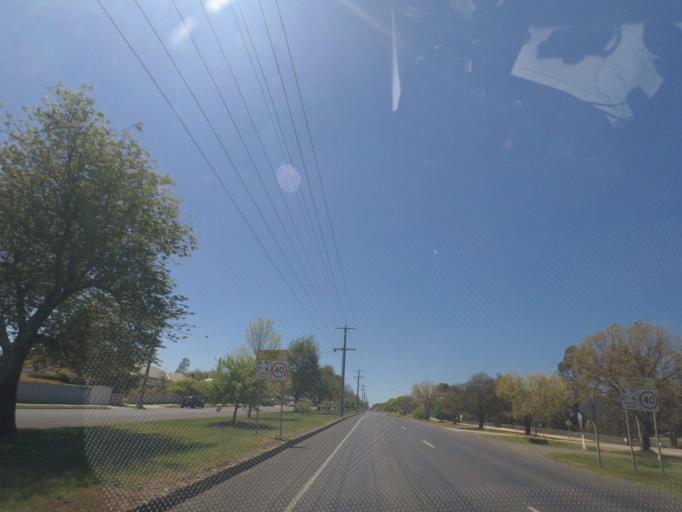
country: AU
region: Victoria
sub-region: Hume
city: Sunbury
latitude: -37.4617
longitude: 144.6780
